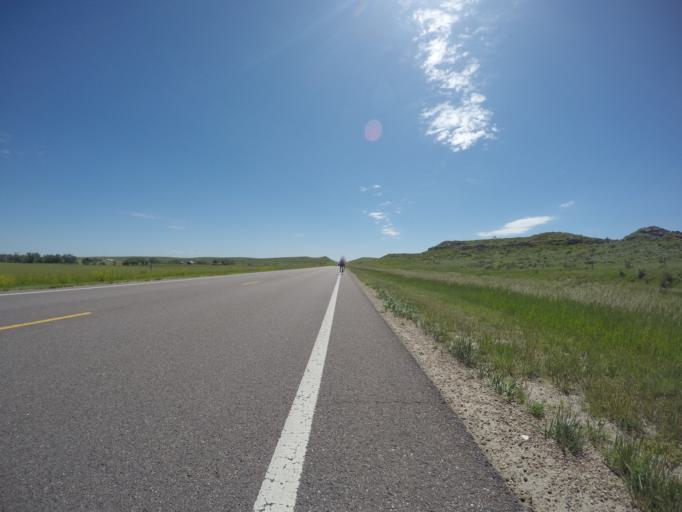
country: US
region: Kansas
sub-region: Rawlins County
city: Atwood
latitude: 39.8134
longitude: -101.0092
